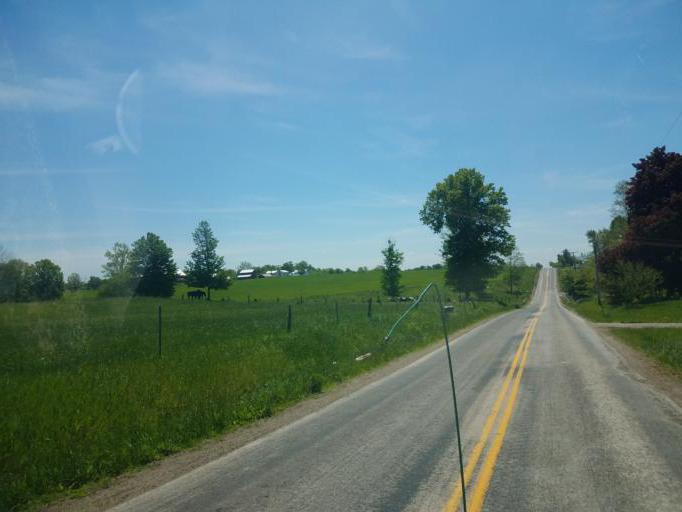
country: US
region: Ohio
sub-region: Ashland County
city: Ashland
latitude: 40.9509
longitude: -82.2437
